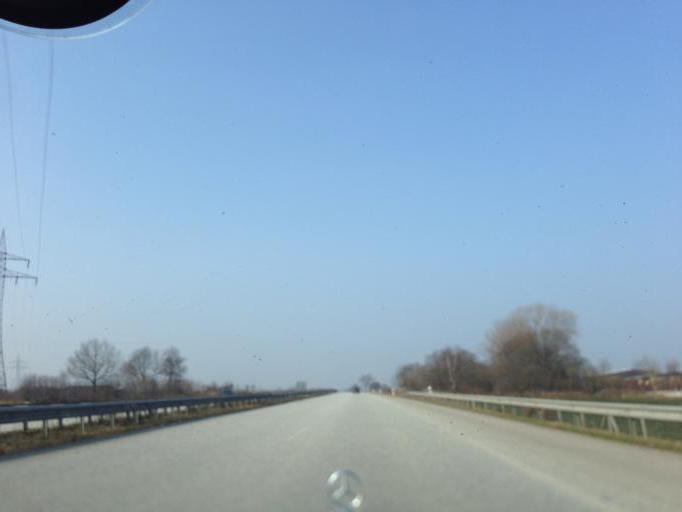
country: DE
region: Schleswig-Holstein
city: Trappenkamp
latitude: 54.0465
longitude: 10.2354
